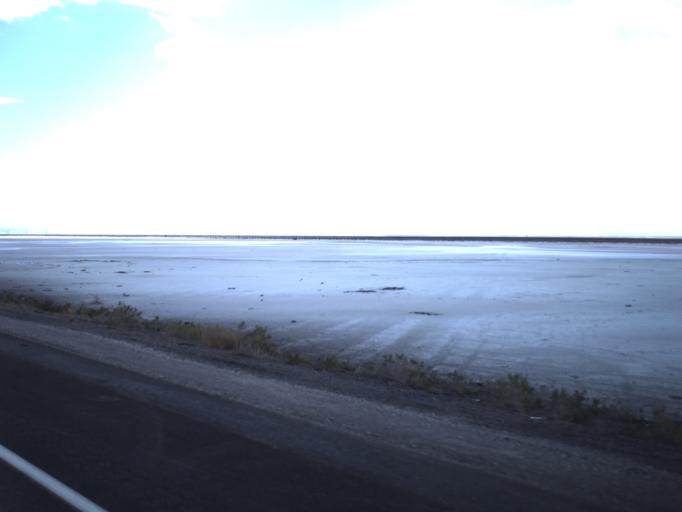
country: US
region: Utah
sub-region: Tooele County
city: Wendover
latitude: 40.7316
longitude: -113.5316
